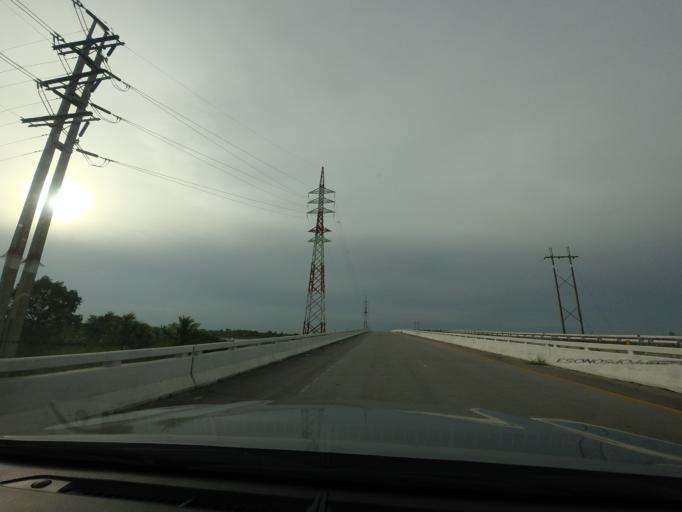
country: TH
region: Nakhon Si Thammarat
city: Hua Sai
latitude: 8.0151
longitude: 100.2962
